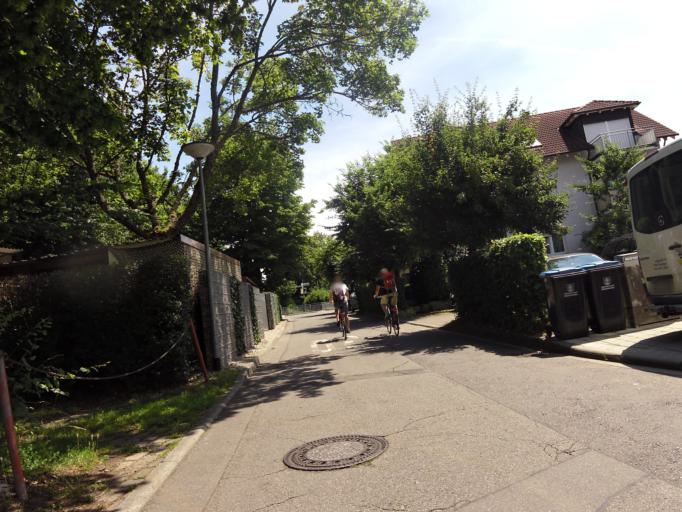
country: DE
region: Baden-Wuerttemberg
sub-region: Tuebingen Region
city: Uberlingen
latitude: 47.7527
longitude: 9.1930
